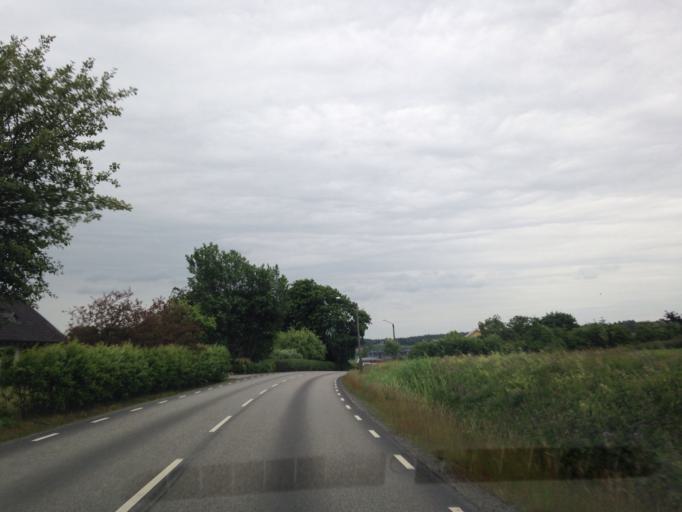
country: SE
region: Vaestra Goetaland
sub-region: Marks Kommun
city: Horred
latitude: 57.4937
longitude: 12.5279
